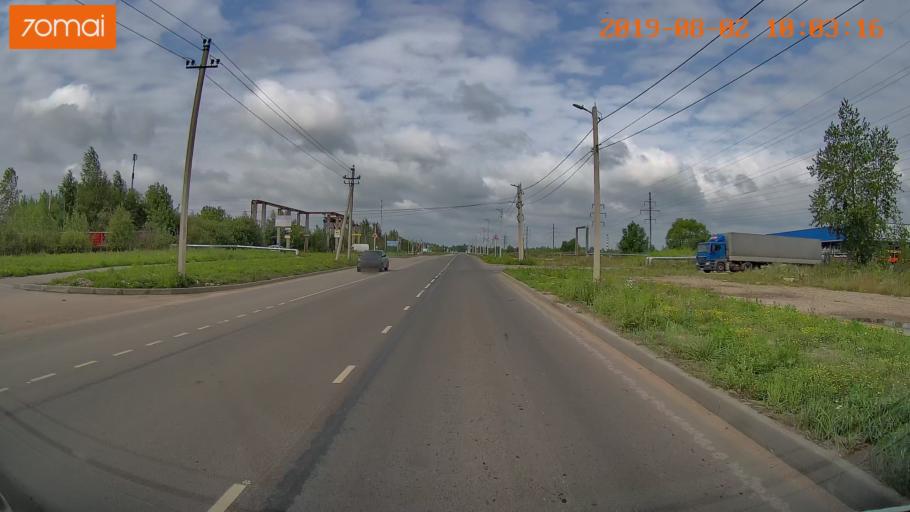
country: RU
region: Ivanovo
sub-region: Gorod Ivanovo
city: Ivanovo
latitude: 56.9662
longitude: 40.9447
